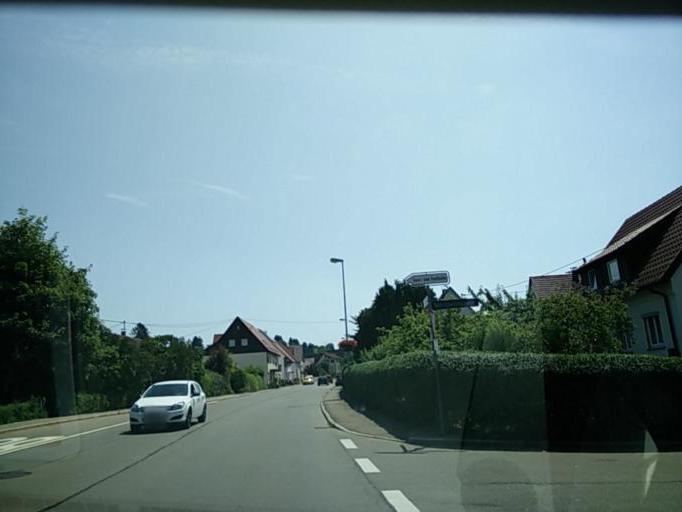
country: DE
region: Baden-Wuerttemberg
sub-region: Tuebingen Region
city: Gomaringen
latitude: 48.4514
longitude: 9.1349
